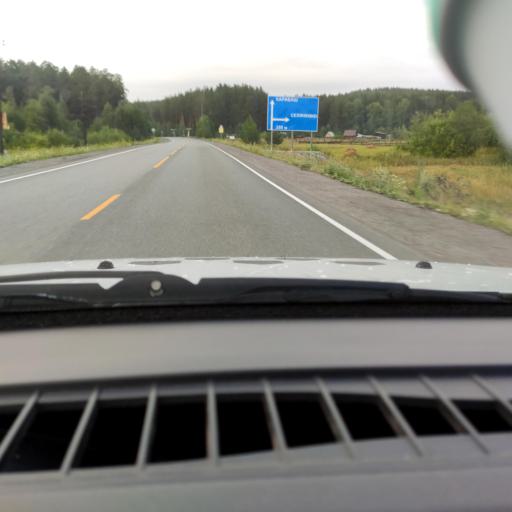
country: RU
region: Chelyabinsk
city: Turgoyak
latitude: 55.2296
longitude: 60.1899
